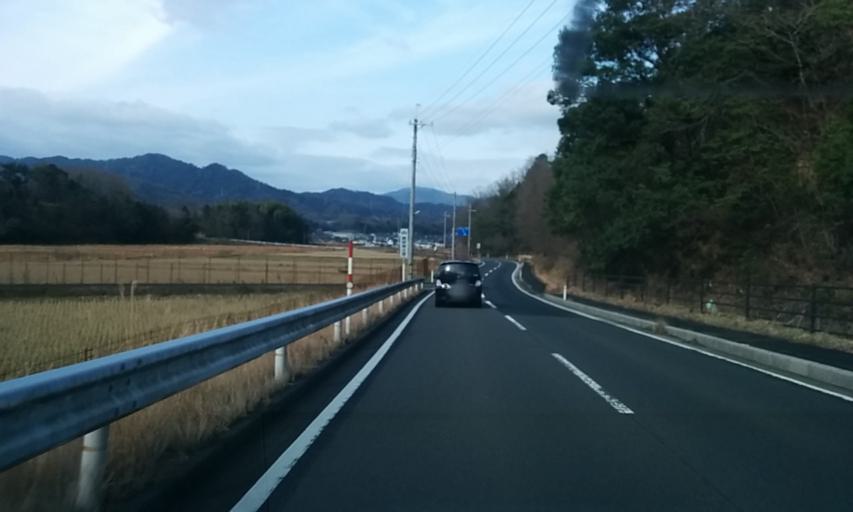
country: JP
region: Kyoto
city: Miyazu
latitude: 35.5833
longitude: 135.1089
